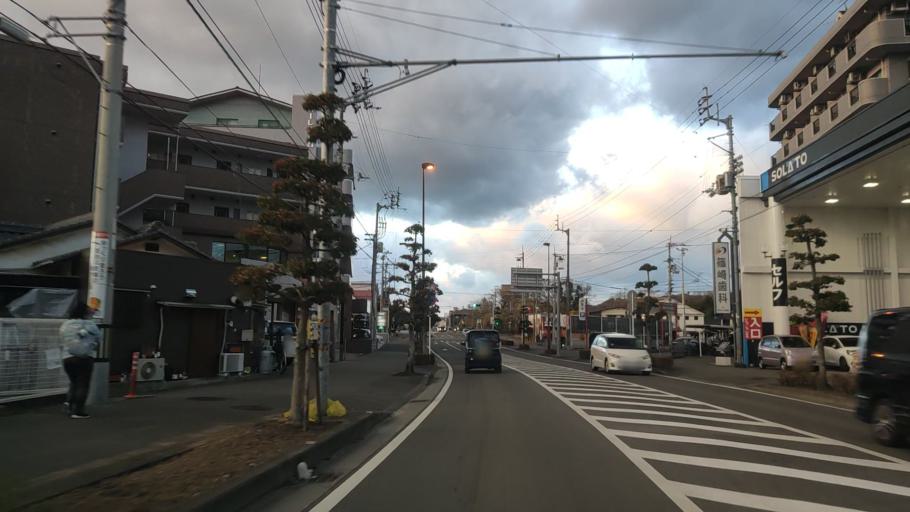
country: JP
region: Ehime
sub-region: Shikoku-chuo Shi
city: Matsuyama
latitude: 33.8379
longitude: 132.7867
